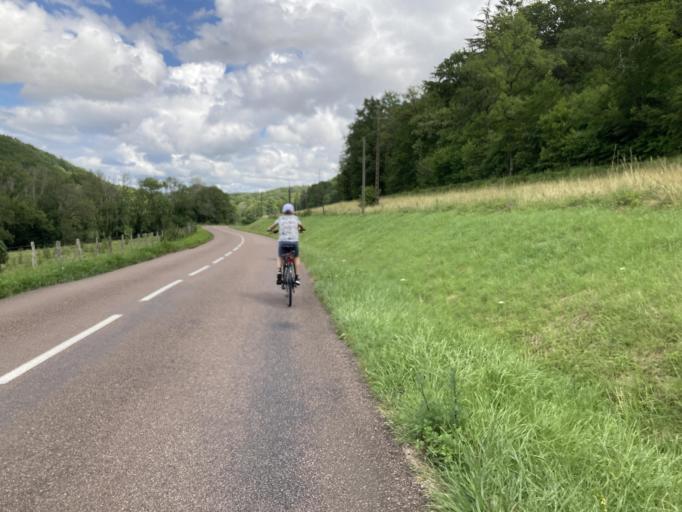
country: FR
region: Bourgogne
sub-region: Departement de la Cote-d'Or
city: Montbard
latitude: 47.6362
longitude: 4.3778
